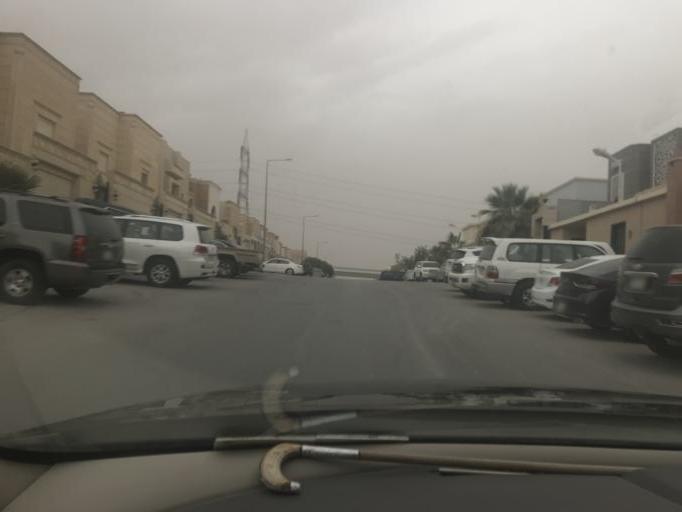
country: SA
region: Ar Riyad
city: Riyadh
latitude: 24.7964
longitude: 46.6918
